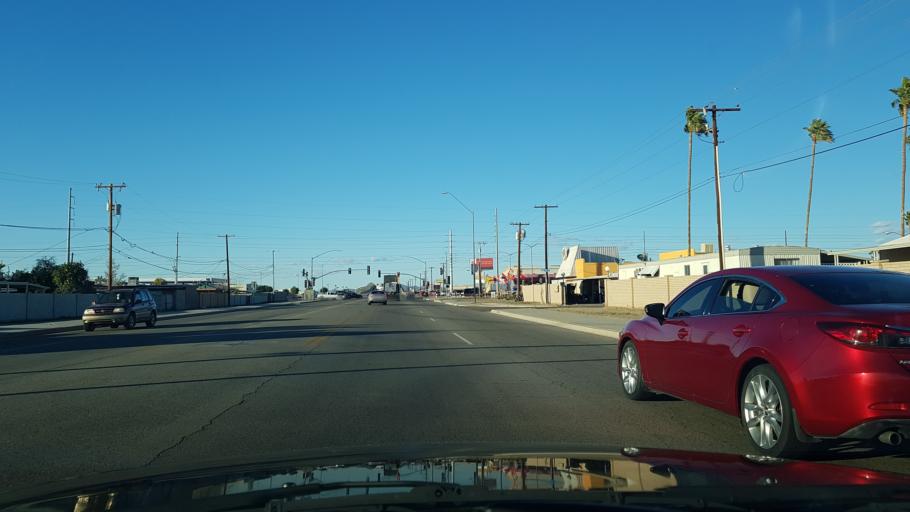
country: US
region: Arizona
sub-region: Yuma County
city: Yuma
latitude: 32.6824
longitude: -114.5988
